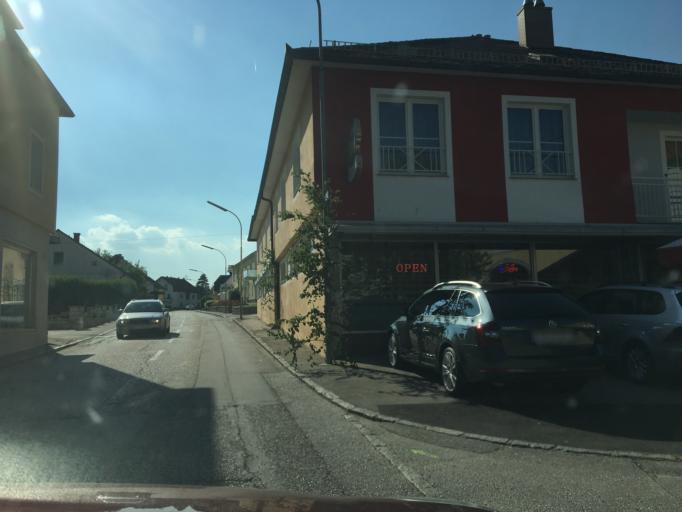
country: AT
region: Lower Austria
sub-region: Politischer Bezirk Amstetten
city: Ennsdorf
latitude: 48.2716
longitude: 14.5265
